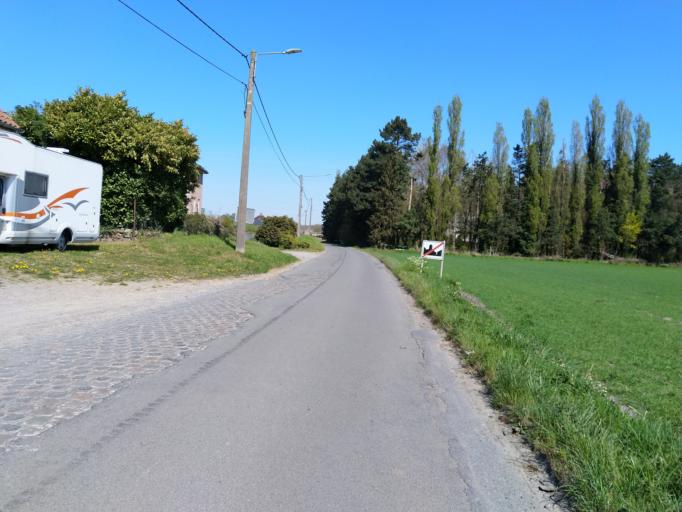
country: BE
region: Wallonia
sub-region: Province du Hainaut
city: Mons
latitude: 50.4810
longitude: 4.0112
